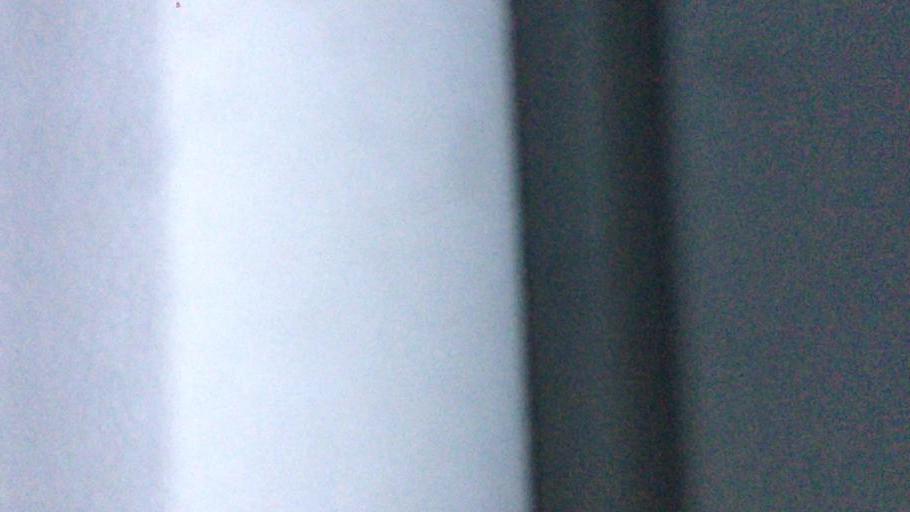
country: US
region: New York
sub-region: Dutchess County
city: Rhinebeck
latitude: 41.9678
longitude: -73.9217
